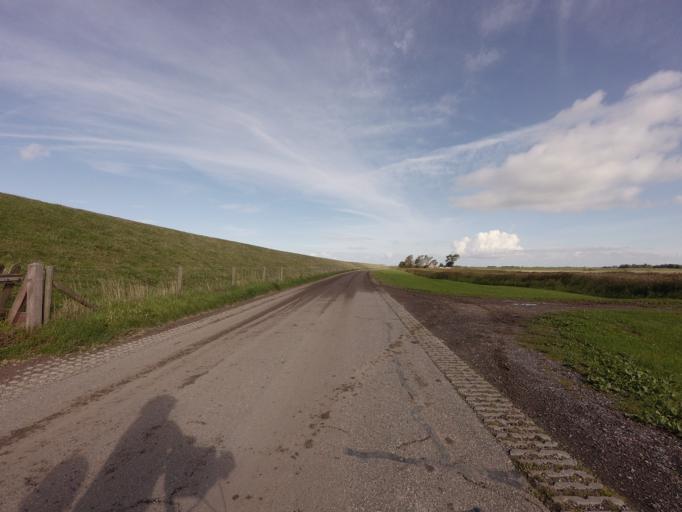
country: NL
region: Friesland
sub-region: Sudwest Fryslan
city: Makkum
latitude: 53.0631
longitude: 5.3934
